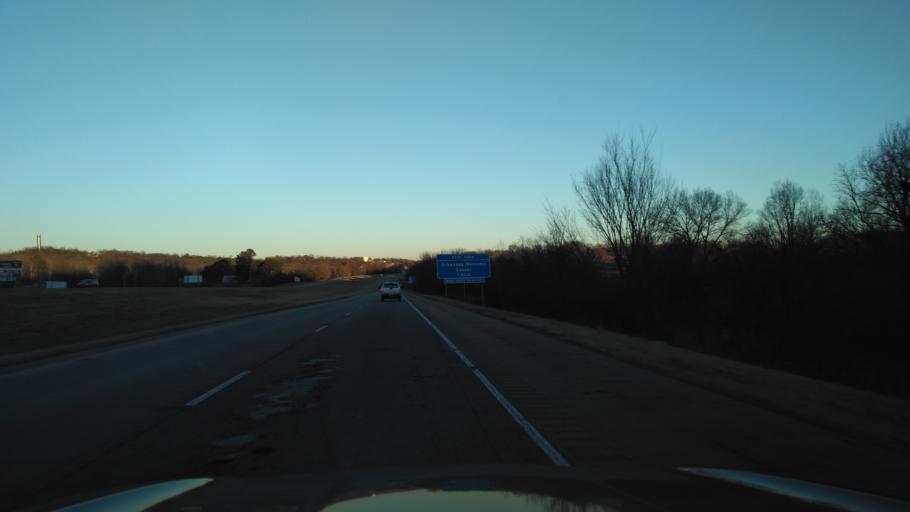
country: US
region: Arkansas
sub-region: Crawford County
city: Van Buren
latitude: 35.4623
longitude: -94.4185
